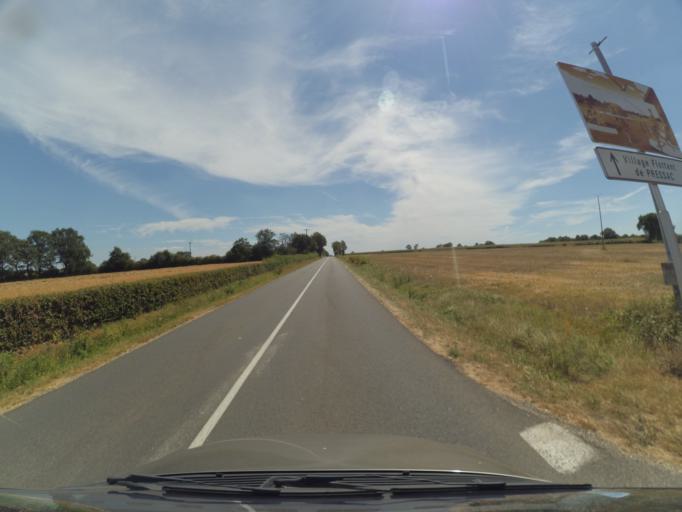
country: FR
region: Poitou-Charentes
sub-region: Departement de la Vienne
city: Availles-Limouzine
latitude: 46.1338
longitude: 0.5581
